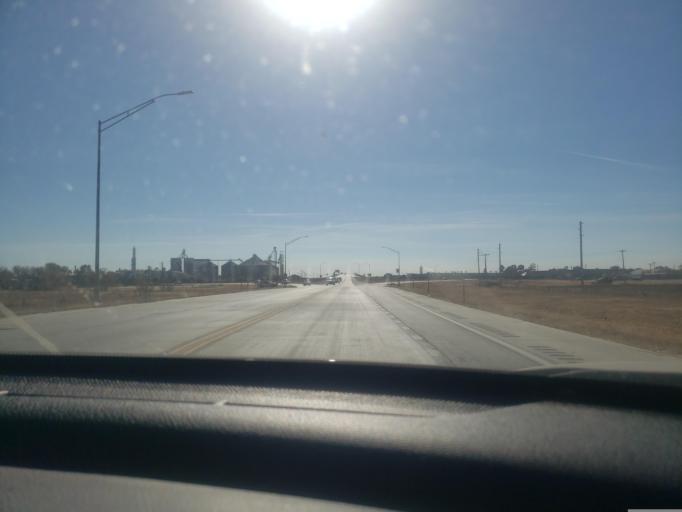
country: US
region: Kansas
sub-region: Finney County
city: Garden City
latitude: 37.9654
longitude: -100.8394
